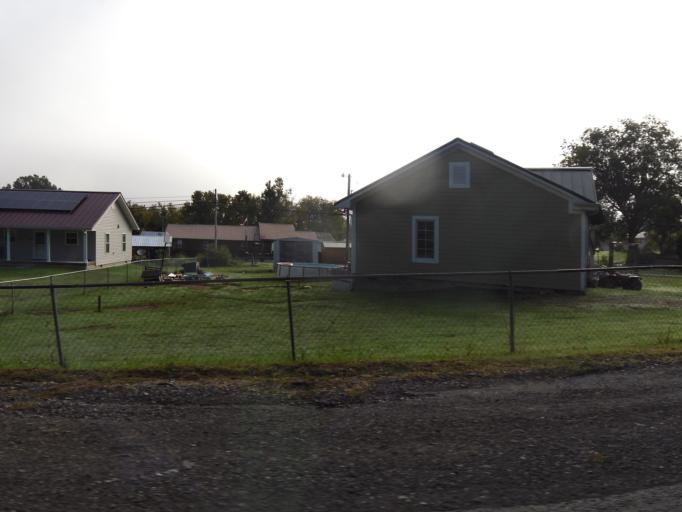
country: US
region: Kentucky
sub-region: Whitley County
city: Williamsburg
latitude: 36.7030
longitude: -84.1454
